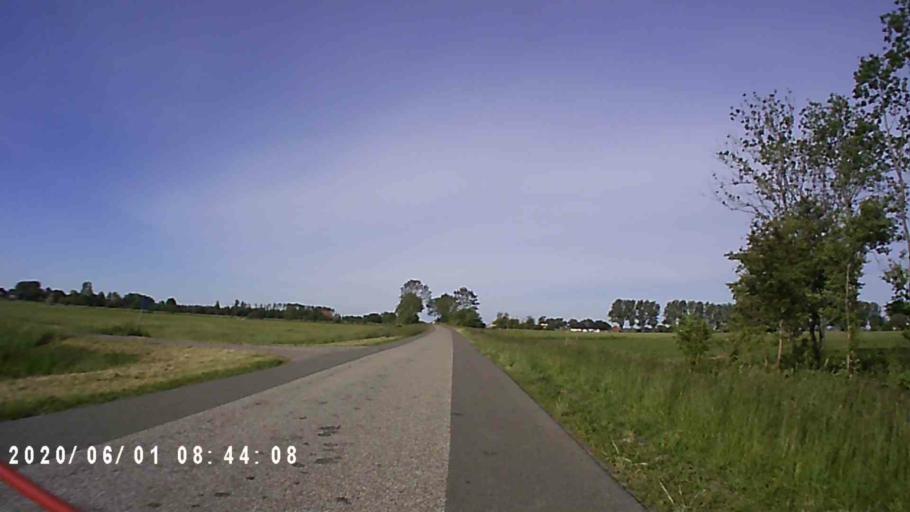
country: NL
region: Friesland
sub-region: Gemeente Ferwerderadiel
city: Burdaard
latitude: 53.2812
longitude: 5.8391
